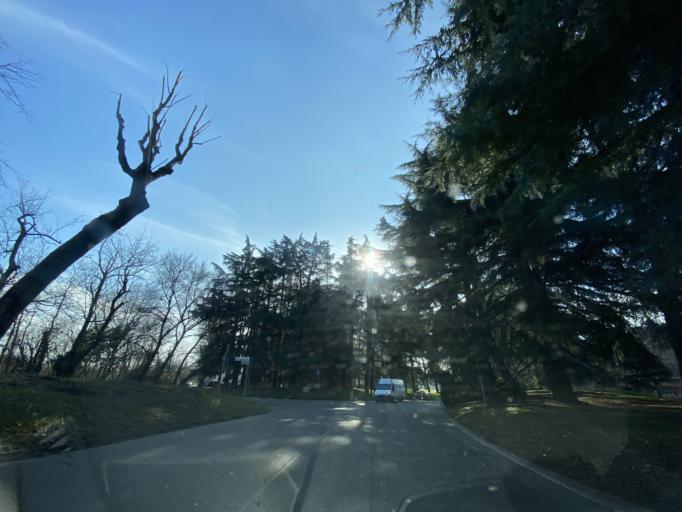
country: IT
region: Lombardy
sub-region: Citta metropolitana di Milano
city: Vimodrone
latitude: 45.5006
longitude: 9.2684
